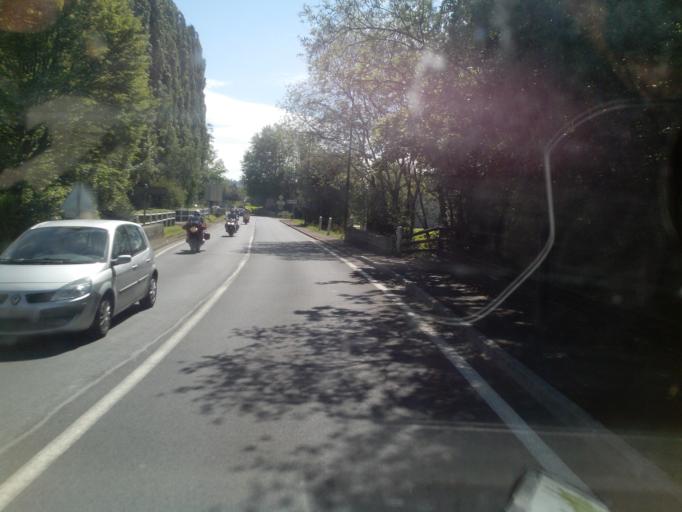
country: FR
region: Lower Normandy
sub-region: Departement du Calvados
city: Saint-Gatien-des-Bois
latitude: 49.2939
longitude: 0.1954
